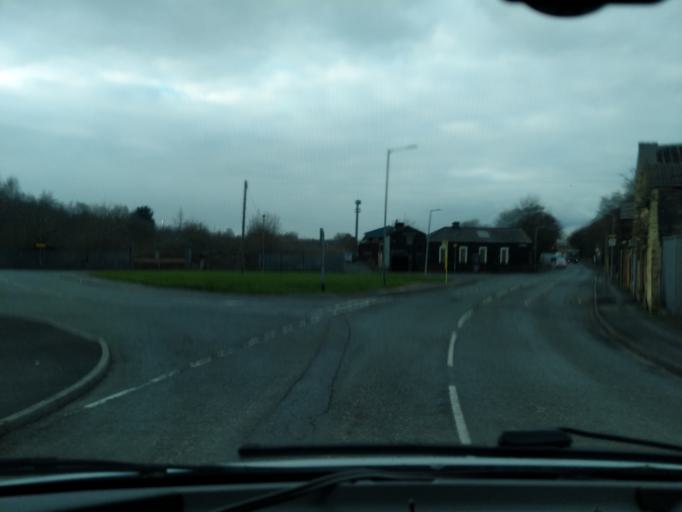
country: GB
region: England
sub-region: St. Helens
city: St Helens
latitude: 53.4398
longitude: -2.7074
